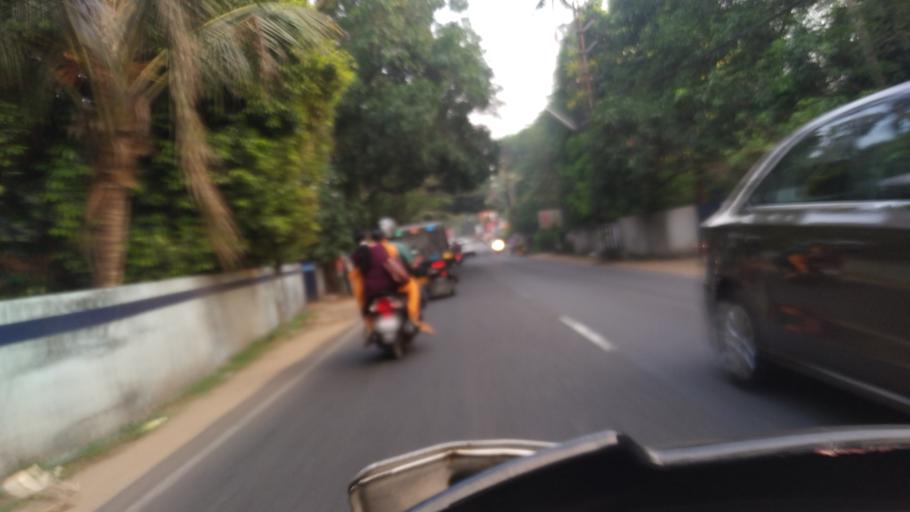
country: IN
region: Kerala
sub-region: Thrissur District
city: Kodungallur
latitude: 10.2399
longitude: 76.1924
